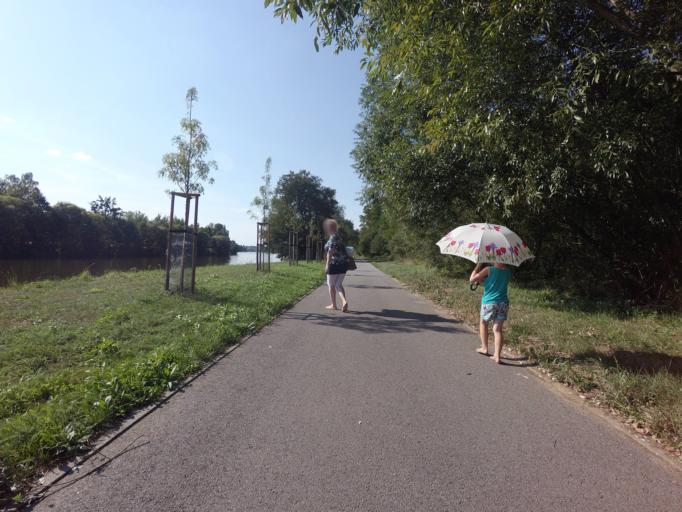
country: CZ
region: Jihocesky
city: Tyn nad Vltavou
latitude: 49.2146
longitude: 14.4376
